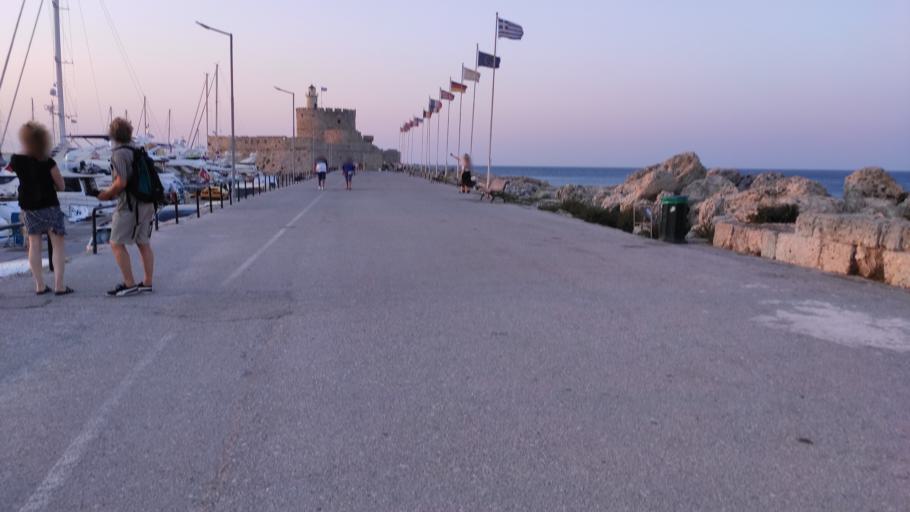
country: GR
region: South Aegean
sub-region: Nomos Dodekanisou
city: Rodos
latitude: 36.4493
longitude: 28.2278
